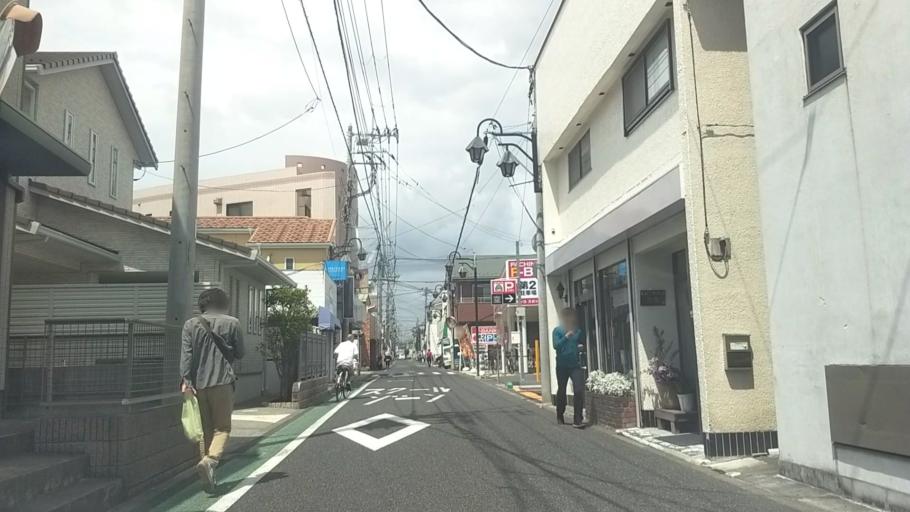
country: JP
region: Kanagawa
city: Fujisawa
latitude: 35.3388
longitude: 139.4509
